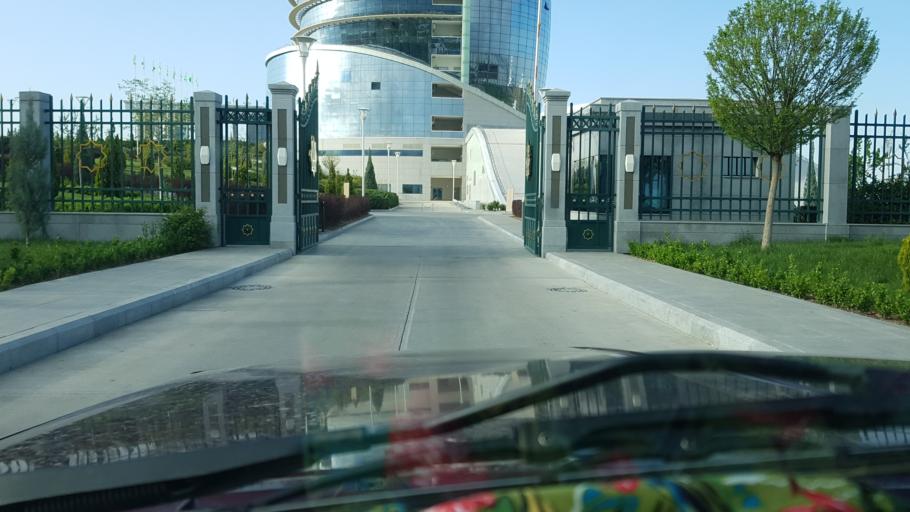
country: TM
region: Ahal
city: Ashgabat
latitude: 37.9279
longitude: 58.3331
